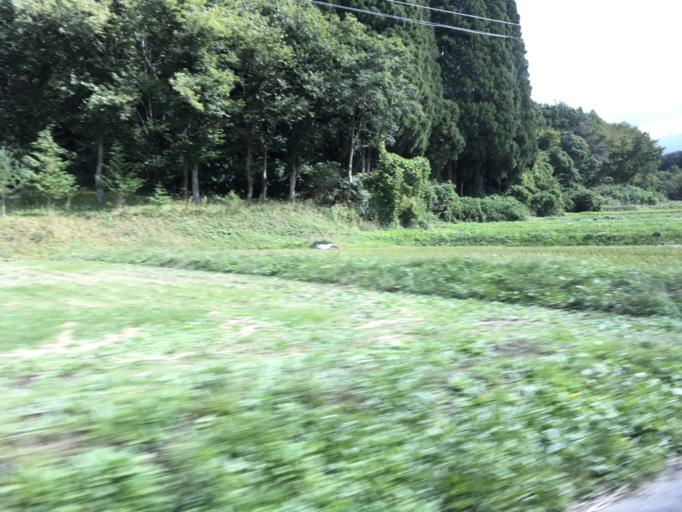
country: JP
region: Iwate
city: Ichinoseki
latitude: 38.8348
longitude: 141.3553
